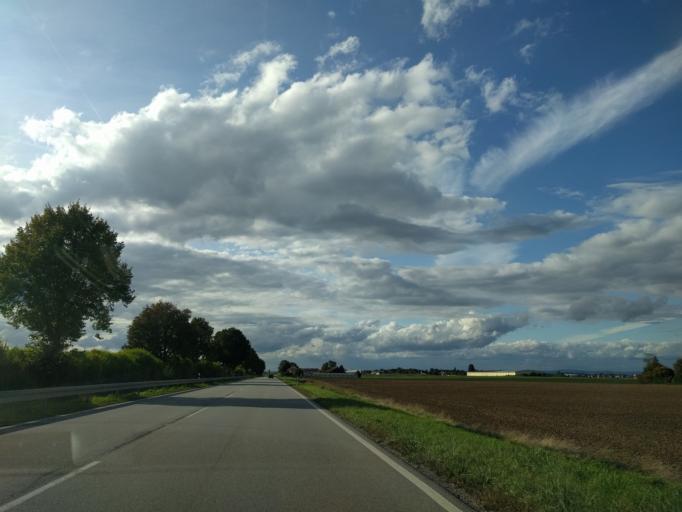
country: DE
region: Bavaria
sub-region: Lower Bavaria
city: Stephansposching
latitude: 48.7968
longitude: 12.8173
